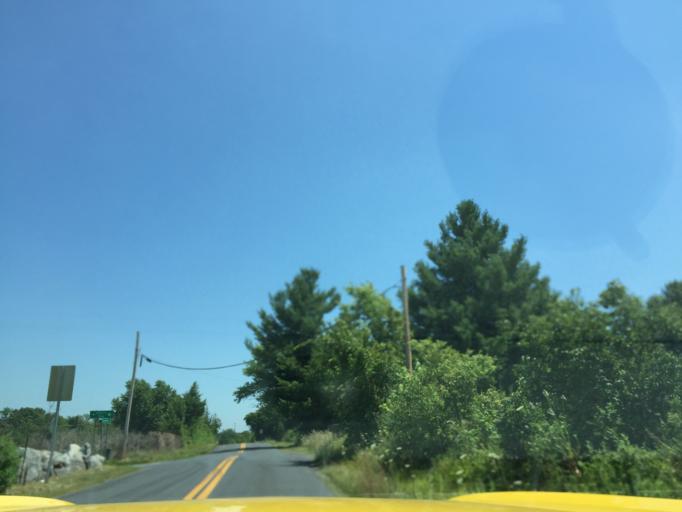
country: US
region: West Virginia
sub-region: Berkeley County
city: Inwood
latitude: 39.3277
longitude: -78.0231
